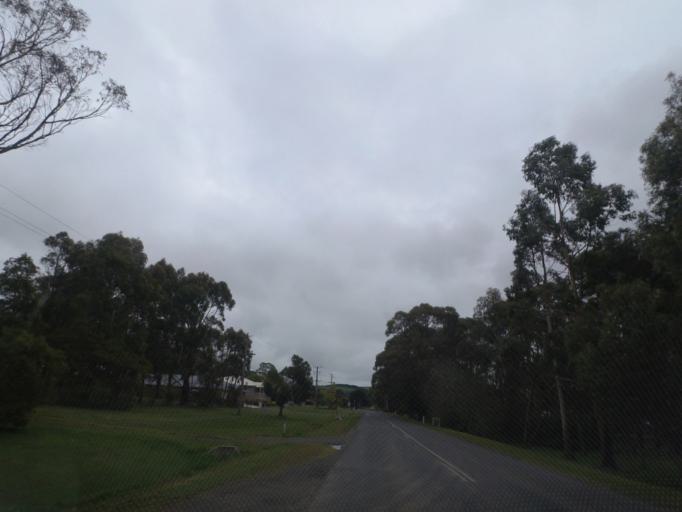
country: AU
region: Victoria
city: Brown Hill
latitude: -37.5847
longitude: 144.1129
